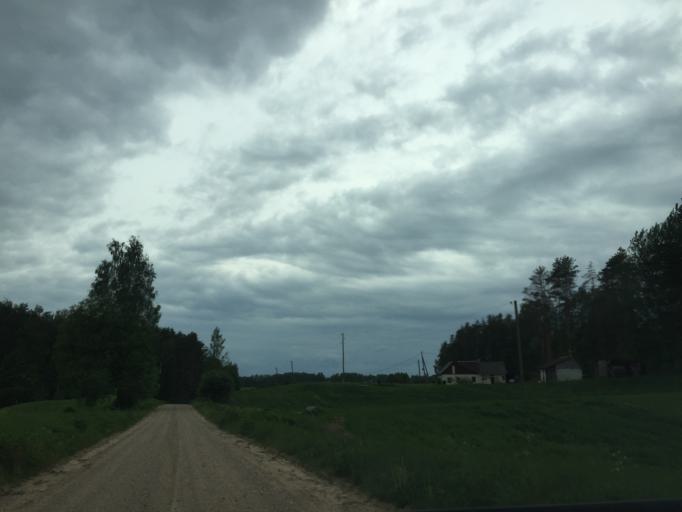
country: LV
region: Aglona
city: Aglona
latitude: 56.1589
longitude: 27.2345
